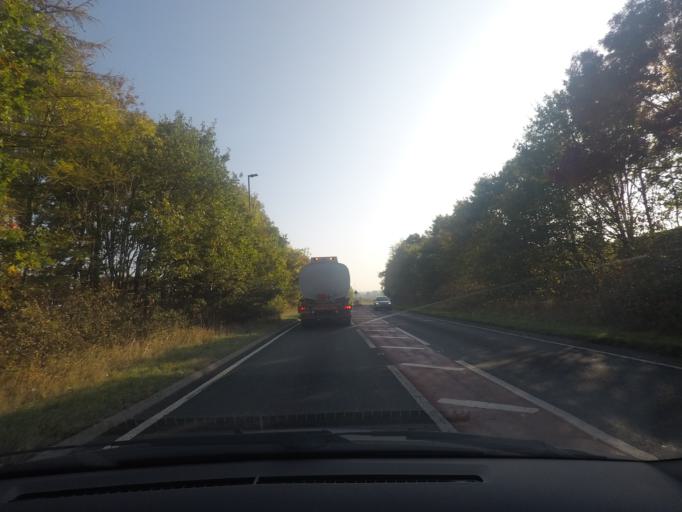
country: GB
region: England
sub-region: City and Borough of Leeds
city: Walton
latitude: 54.0028
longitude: -1.2982
